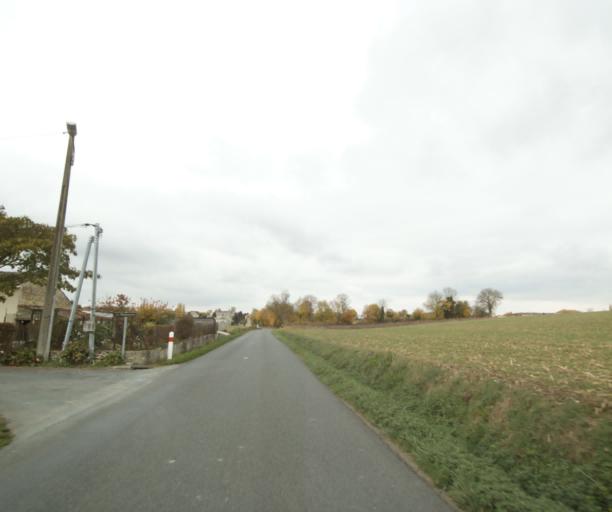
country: FR
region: Poitou-Charentes
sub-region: Departement de la Charente-Maritime
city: Bussac-sur-Charente
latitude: 45.7789
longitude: -0.6732
